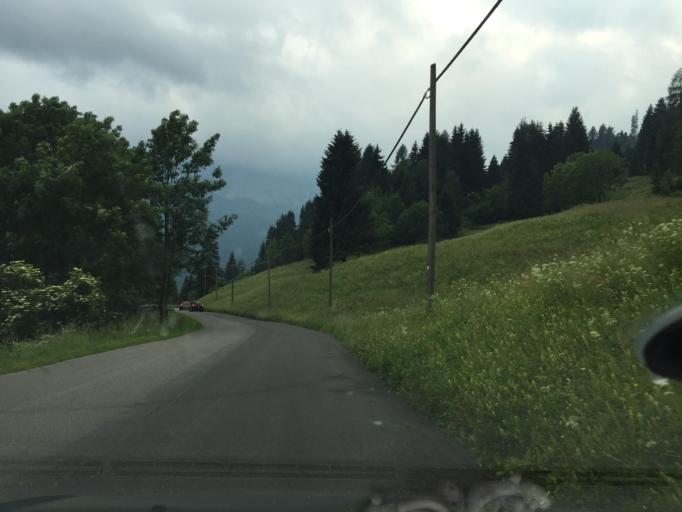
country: IT
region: Friuli Venezia Giulia
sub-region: Provincia di Udine
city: Rigolato
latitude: 46.5811
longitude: 12.8171
